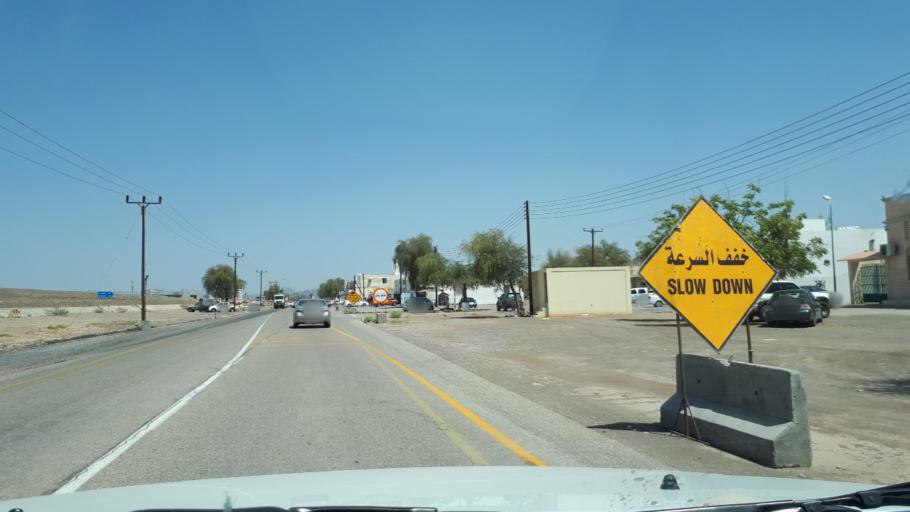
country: OM
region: Ash Sharqiyah
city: Al Qabil
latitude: 22.6051
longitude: 58.6681
